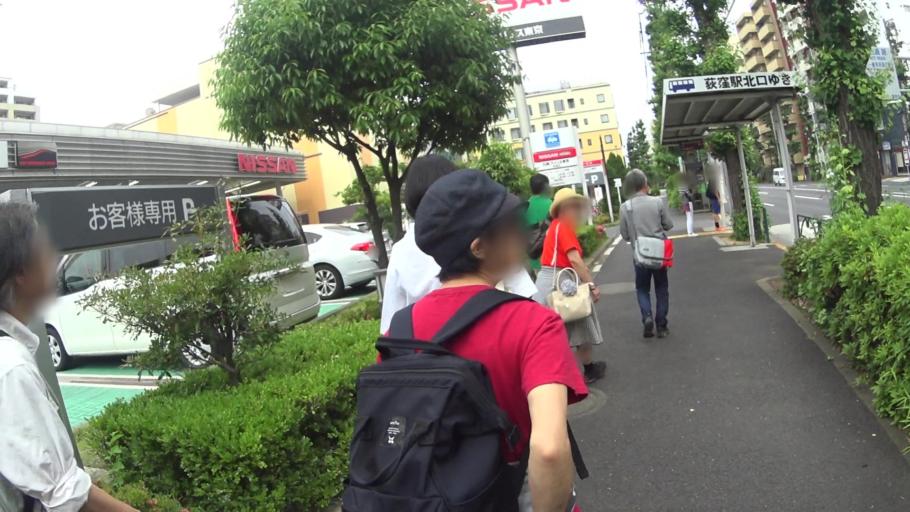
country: JP
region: Tokyo
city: Musashino
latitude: 35.7117
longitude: 139.6045
